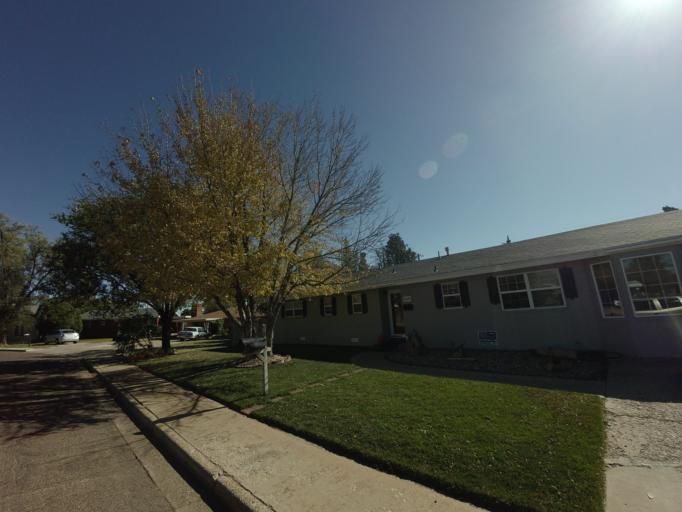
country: US
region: New Mexico
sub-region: Curry County
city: Clovis
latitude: 34.4224
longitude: -103.1995
